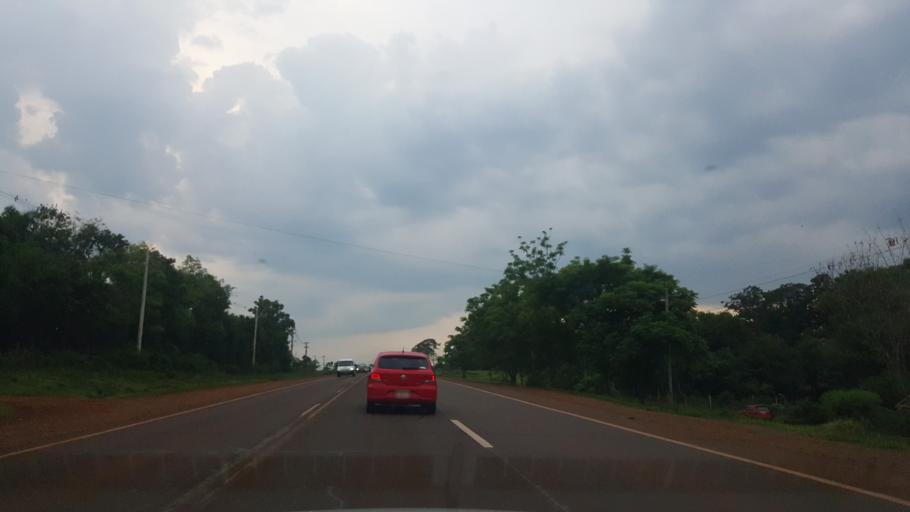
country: AR
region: Misiones
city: Santo Pipo
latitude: -27.1482
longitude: -55.4133
